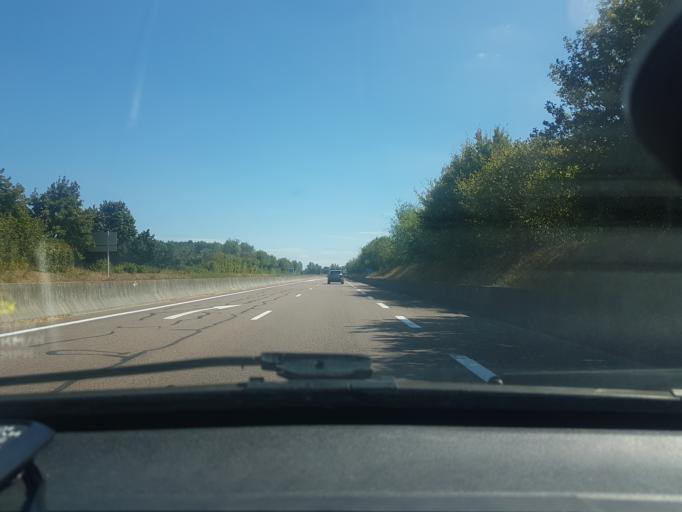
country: FR
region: Bourgogne
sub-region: Departement de la Cote-d'Or
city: Couternon
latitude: 47.3451
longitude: 5.1483
